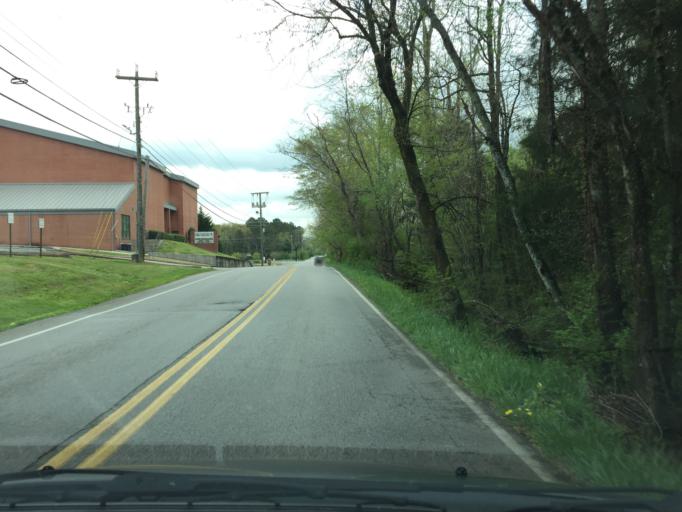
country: US
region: Tennessee
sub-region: Hamilton County
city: Falling Water
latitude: 35.1533
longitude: -85.2437
